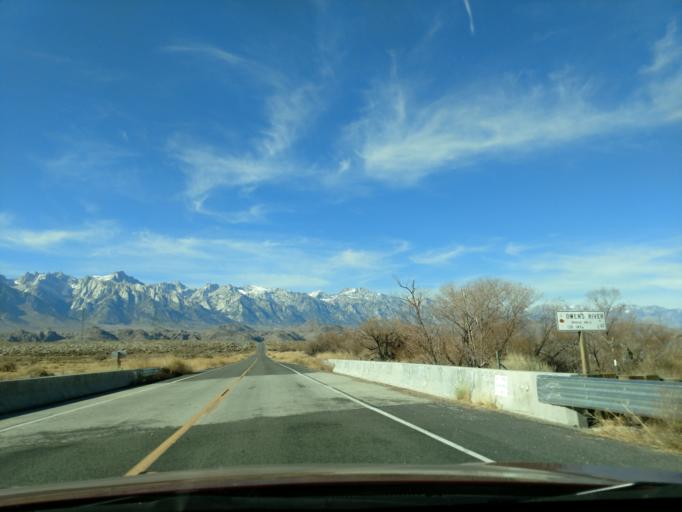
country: US
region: California
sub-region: Inyo County
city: Lone Pine
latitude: 36.5744
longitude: -118.0105
